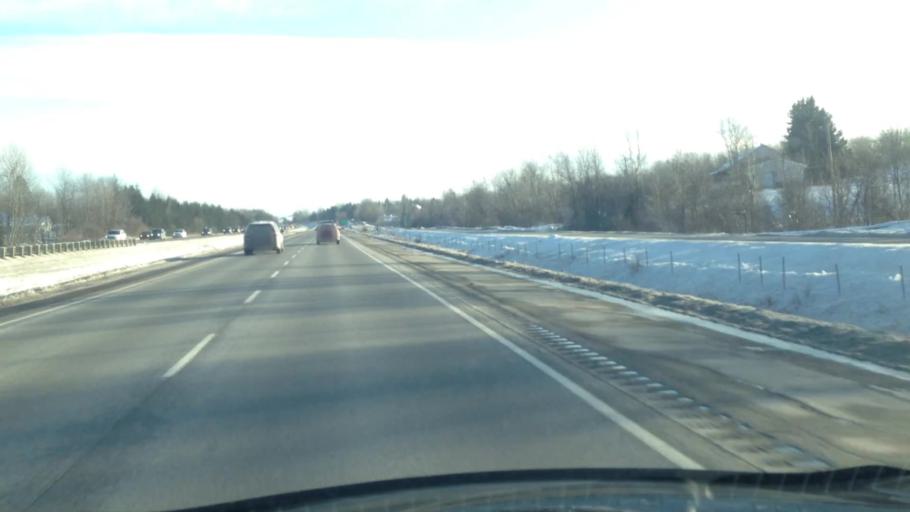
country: CA
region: Quebec
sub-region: Laurentides
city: Prevost
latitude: 45.8212
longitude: -74.0556
